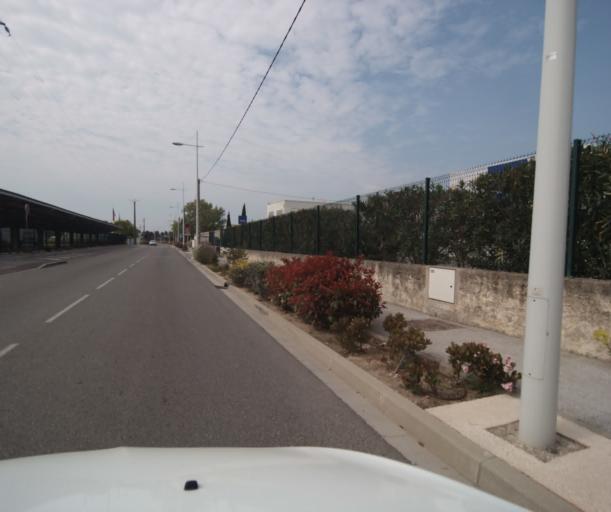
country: FR
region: Provence-Alpes-Cote d'Azur
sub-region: Departement du Var
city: La Farlede
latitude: 43.1463
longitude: 6.0373
